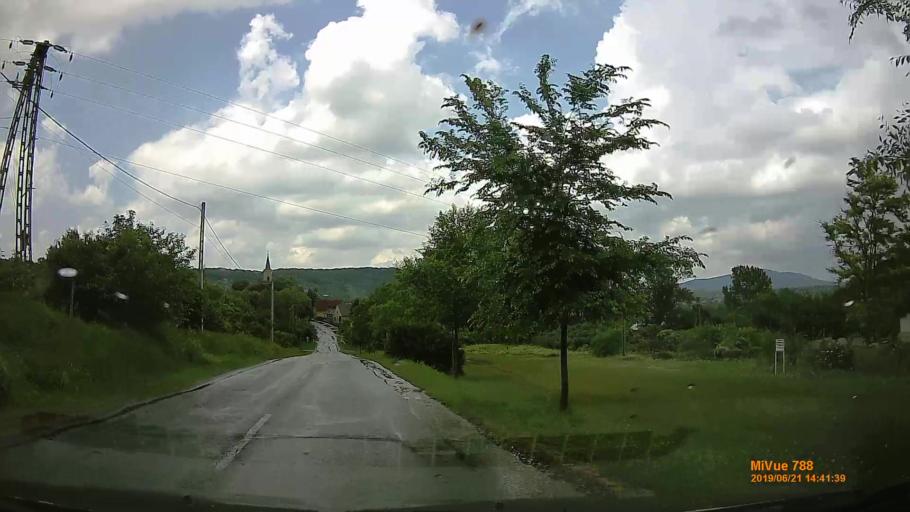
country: HU
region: Baranya
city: Hosszuheteny
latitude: 46.1176
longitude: 18.3115
